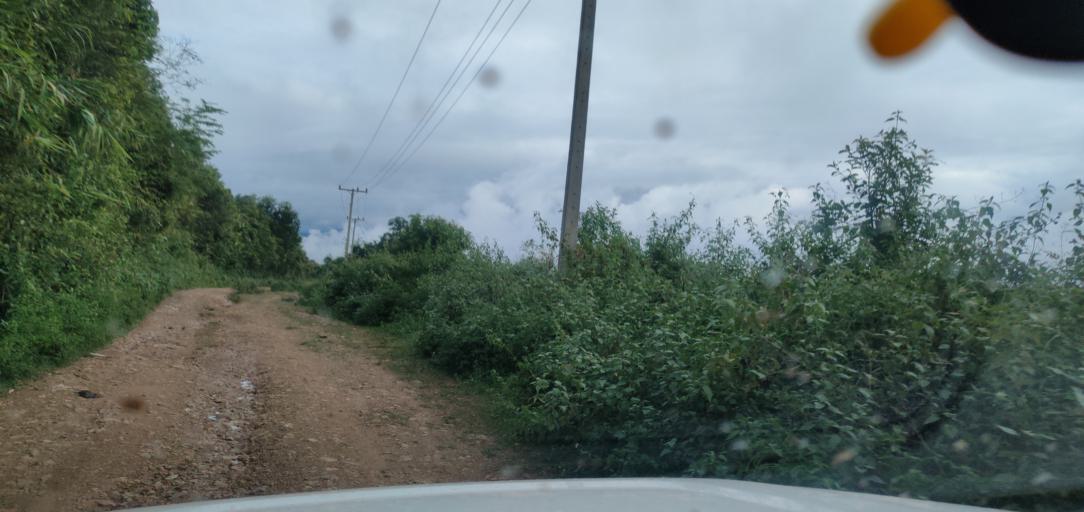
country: LA
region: Phongsali
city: Phongsali
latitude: 21.4450
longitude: 102.2932
